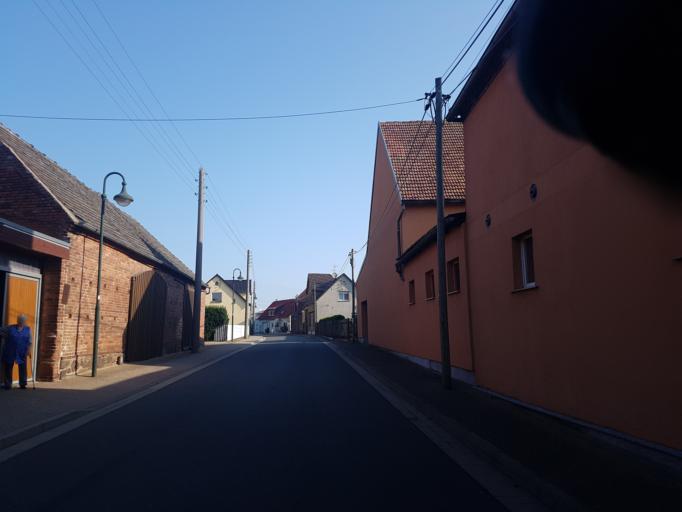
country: DE
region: Saxony-Anhalt
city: Kropstadt
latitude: 51.9895
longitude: 12.6830
